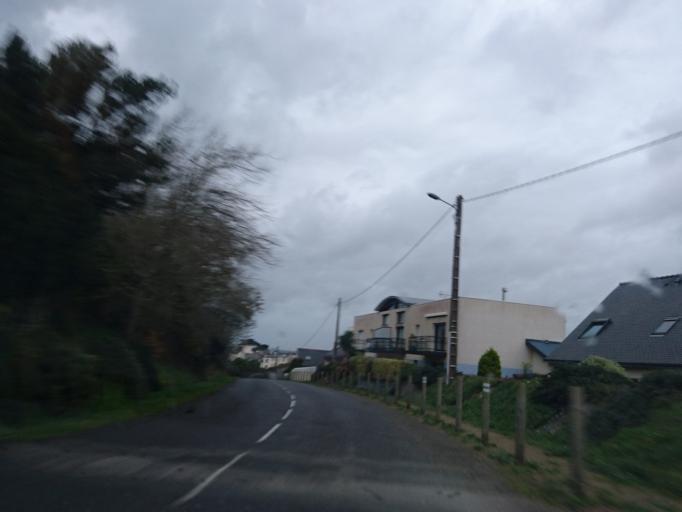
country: FR
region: Brittany
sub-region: Departement du Finistere
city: Le Conquet
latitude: 48.3552
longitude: -4.7752
